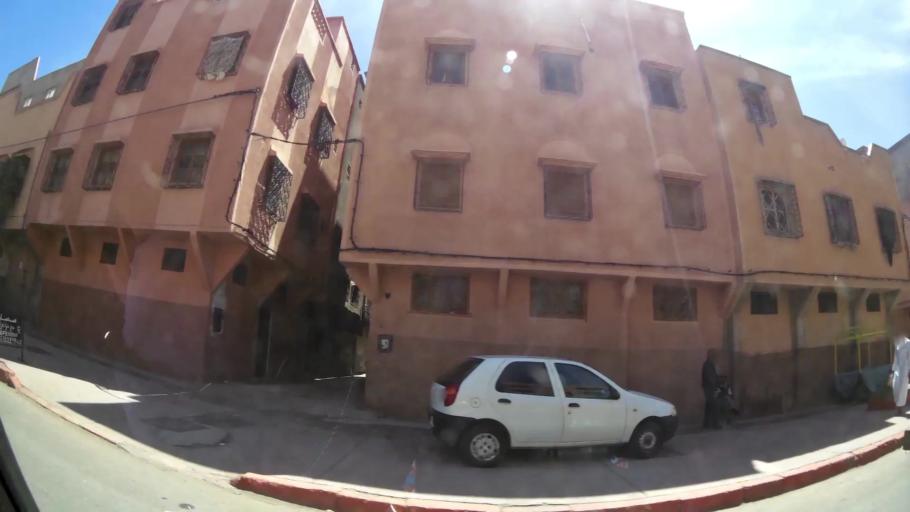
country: MA
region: Marrakech-Tensift-Al Haouz
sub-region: Marrakech
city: Marrakesh
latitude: 31.6589
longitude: -7.9949
